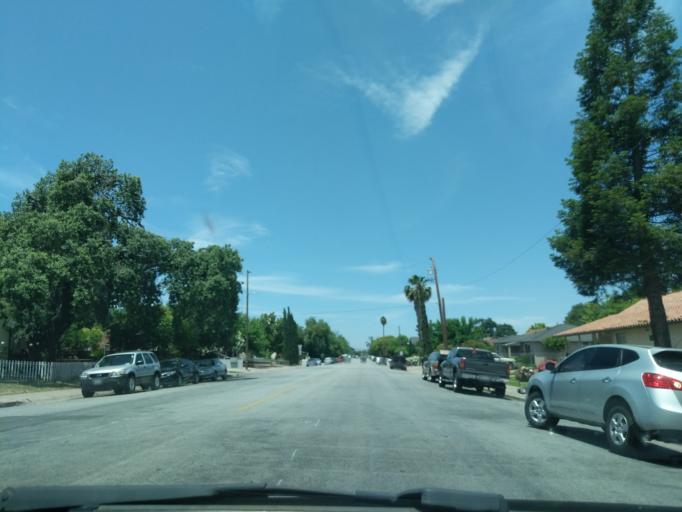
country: US
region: California
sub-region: Santa Clara County
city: Gilroy
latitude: 37.0150
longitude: -121.5751
